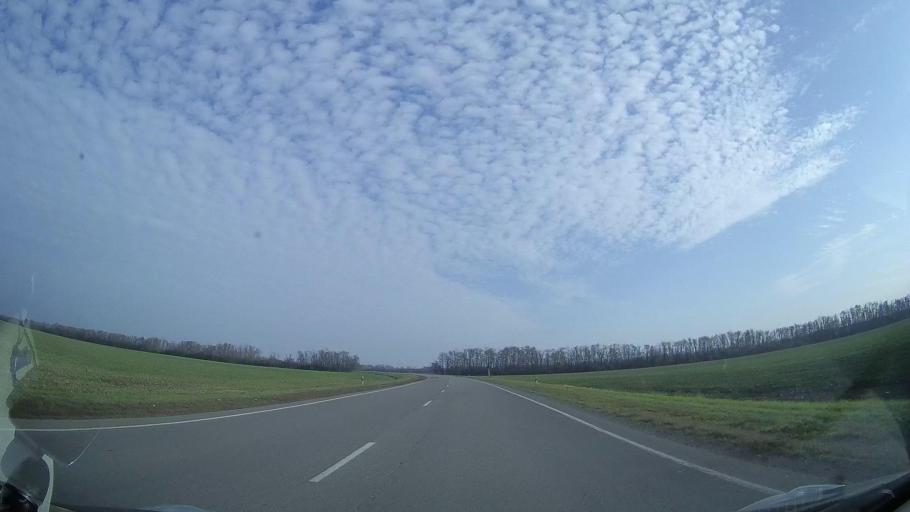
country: RU
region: Rostov
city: Tselina
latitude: 46.5212
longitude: 41.1539
